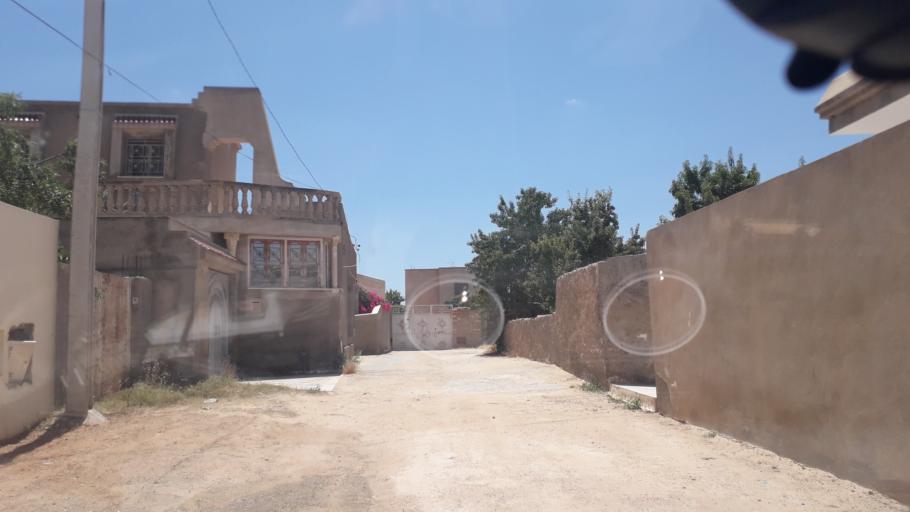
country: TN
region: Safaqis
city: Al Qarmadah
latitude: 34.8169
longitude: 10.7667
